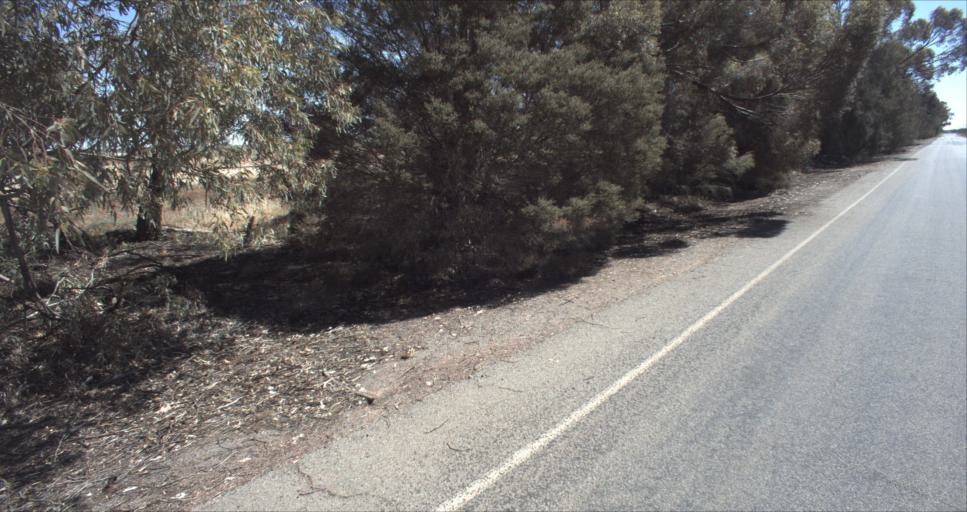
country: AU
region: New South Wales
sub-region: Leeton
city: Leeton
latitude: -34.4697
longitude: 146.2926
